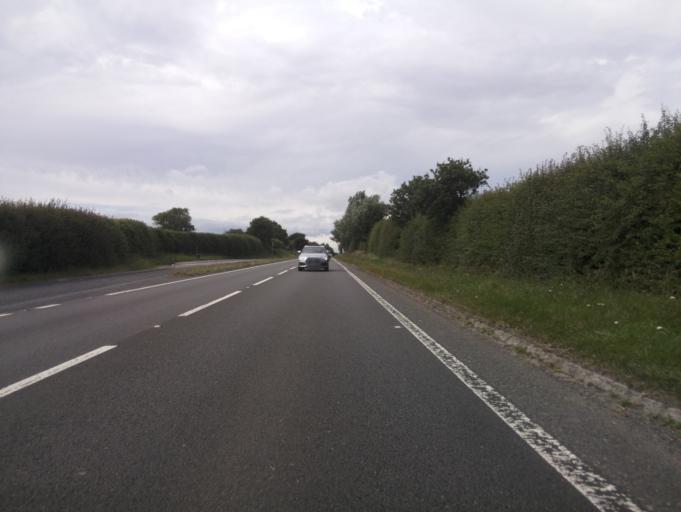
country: GB
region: England
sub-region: Somerset
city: Yeovil
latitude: 50.8789
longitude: -2.6022
